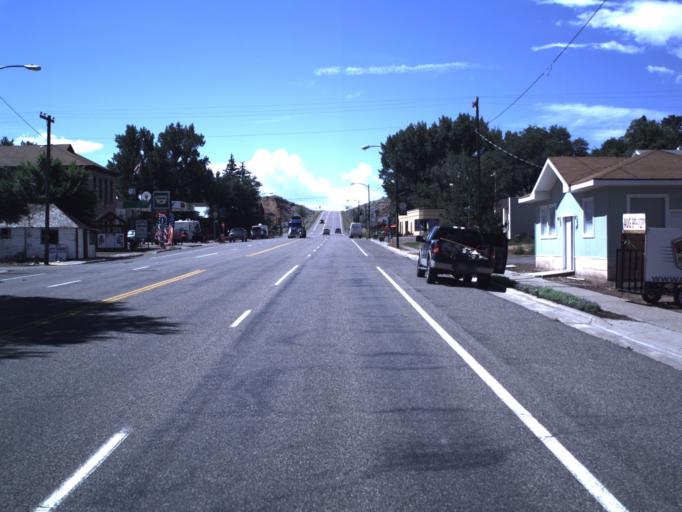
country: US
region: Utah
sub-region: Sevier County
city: Monroe
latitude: 38.4507
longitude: -112.2305
